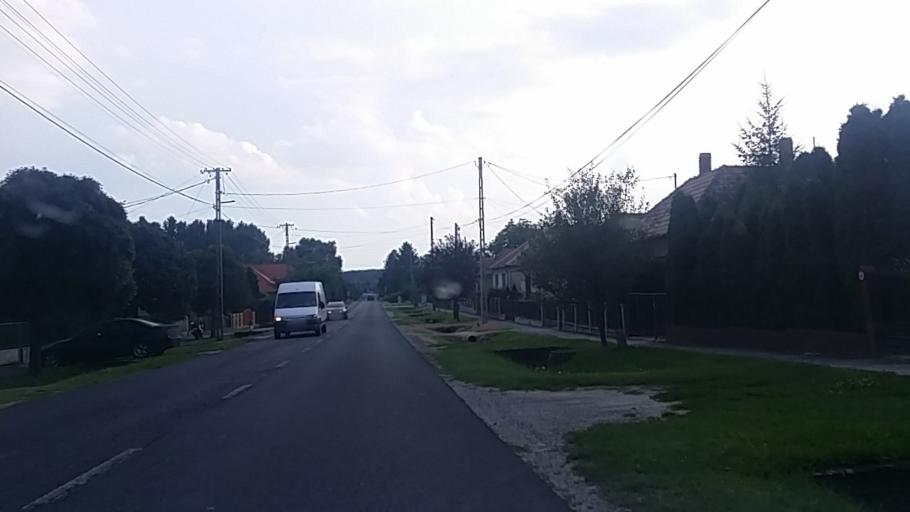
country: HU
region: Zala
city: Sarmellek
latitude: 46.7048
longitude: 17.1678
